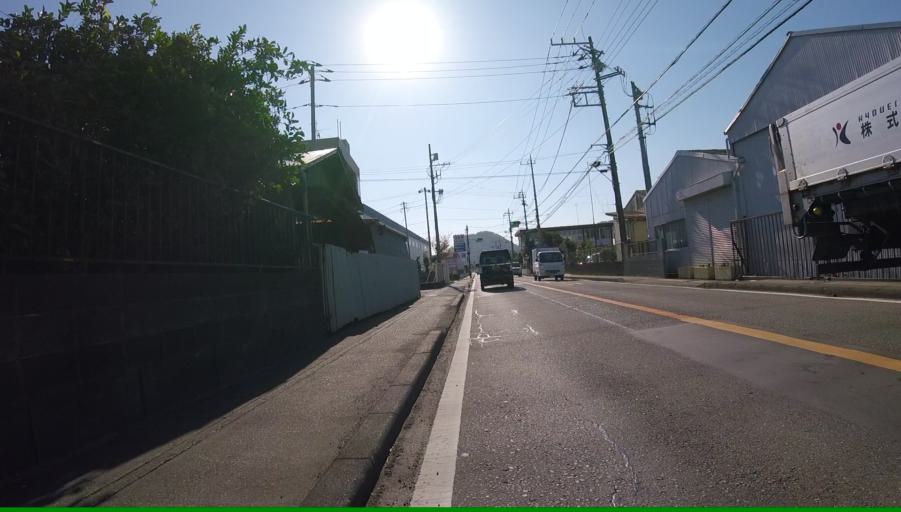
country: JP
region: Shizuoka
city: Mishima
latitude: 35.0834
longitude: 138.9201
